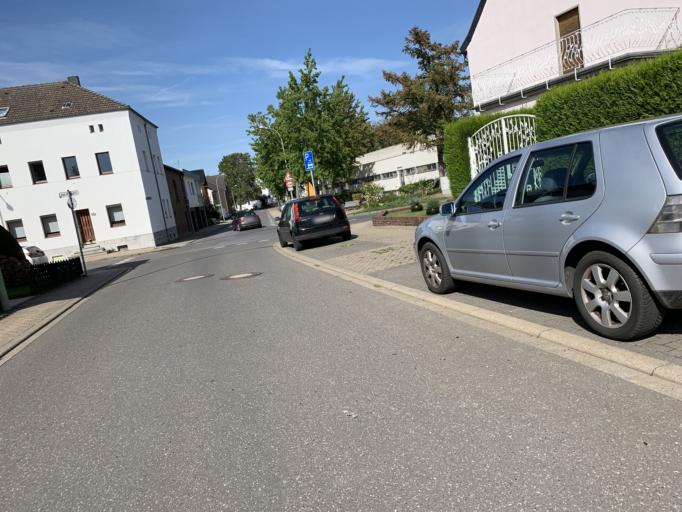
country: DE
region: North Rhine-Westphalia
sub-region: Regierungsbezirk Koln
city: Dueren
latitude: 50.7932
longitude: 6.4501
